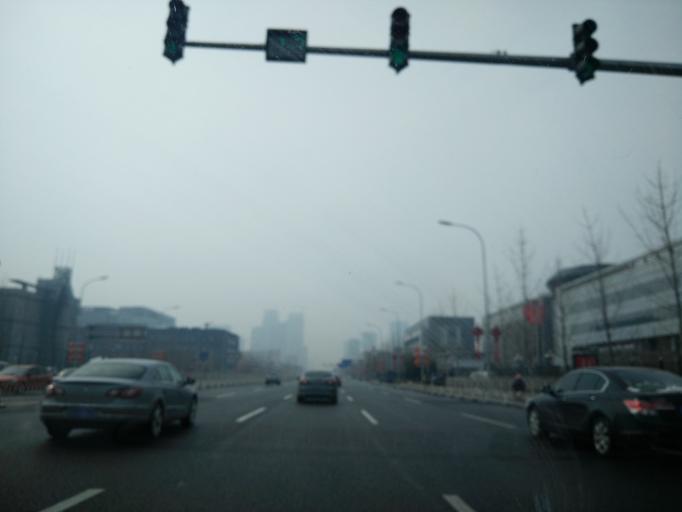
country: CN
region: Beijing
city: Jiugong
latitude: 39.7987
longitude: 116.5183
